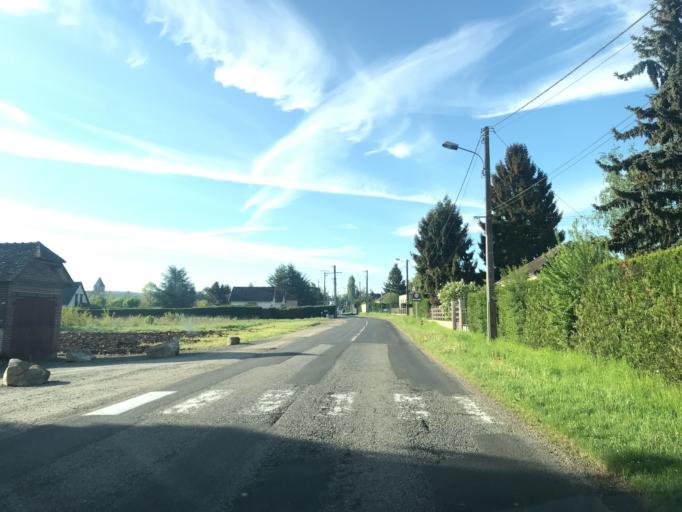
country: FR
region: Haute-Normandie
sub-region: Departement de l'Eure
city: Marcilly-sur-Eure
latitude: 48.7946
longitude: 1.3606
